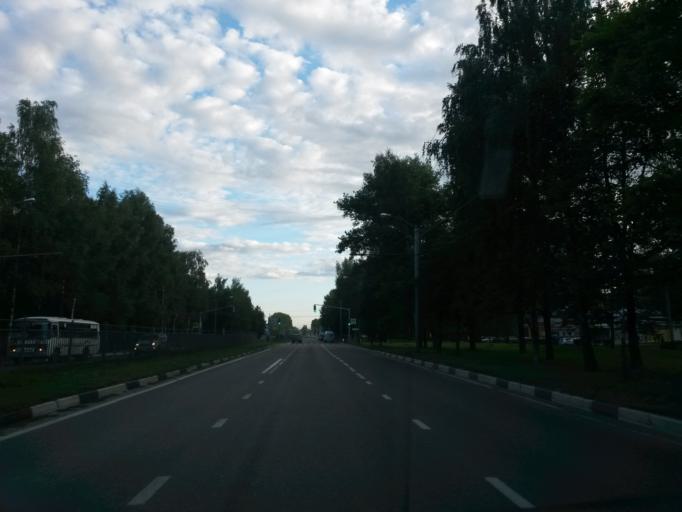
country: RU
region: Jaroslavl
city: Yaroslavl
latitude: 57.6781
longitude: 39.7771
